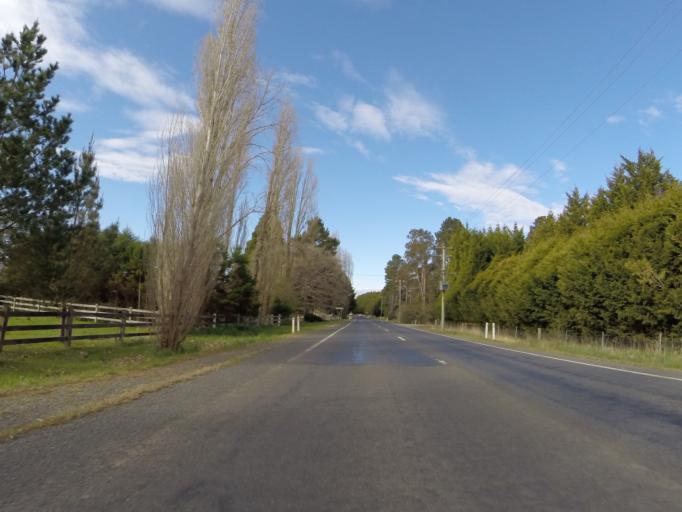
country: AU
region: New South Wales
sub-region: Wingecarribee
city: Moss Vale
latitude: -34.5787
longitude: 150.3057
